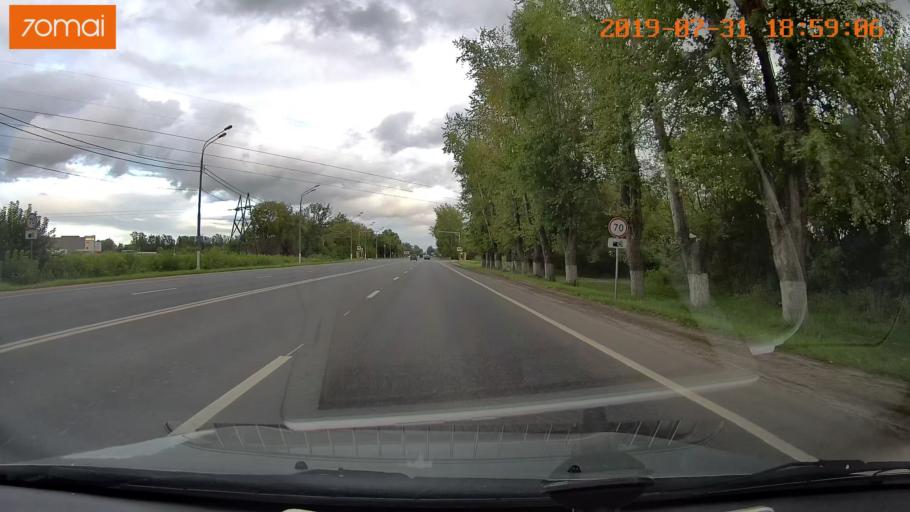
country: RU
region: Moskovskaya
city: Raduzhnyy
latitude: 55.1415
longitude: 38.7121
